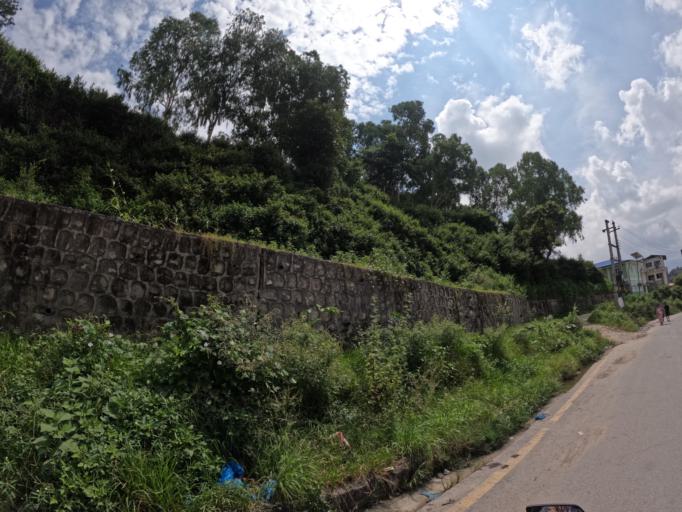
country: NP
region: Central Region
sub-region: Bagmati Zone
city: Bhaktapur
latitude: 27.6799
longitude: 85.3833
